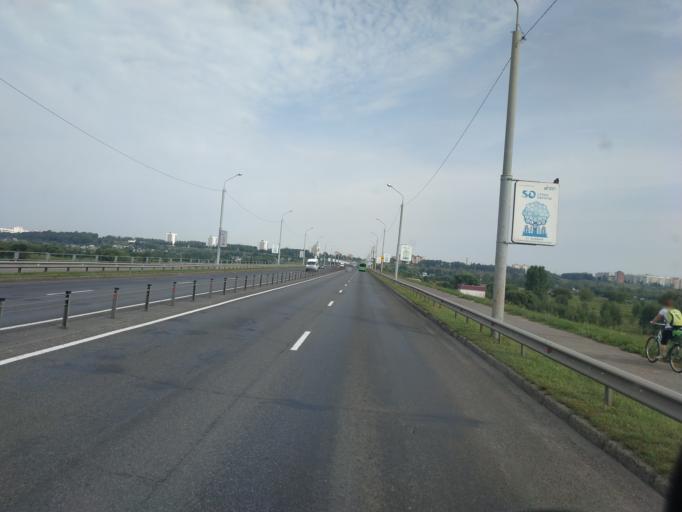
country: BY
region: Mogilev
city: Mahilyow
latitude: 53.8878
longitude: 30.3776
